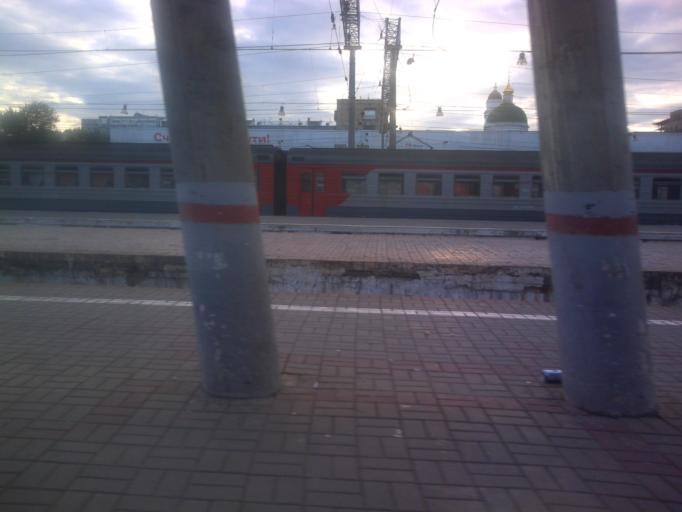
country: RU
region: Moscow
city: Zamoskvorech'ye
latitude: 55.7283
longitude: 37.6412
